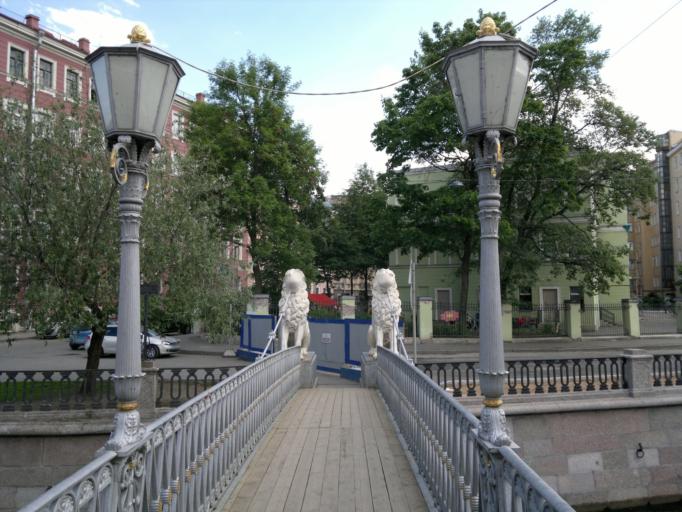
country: RU
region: St.-Petersburg
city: Saint Petersburg
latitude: 59.9269
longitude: 30.3014
